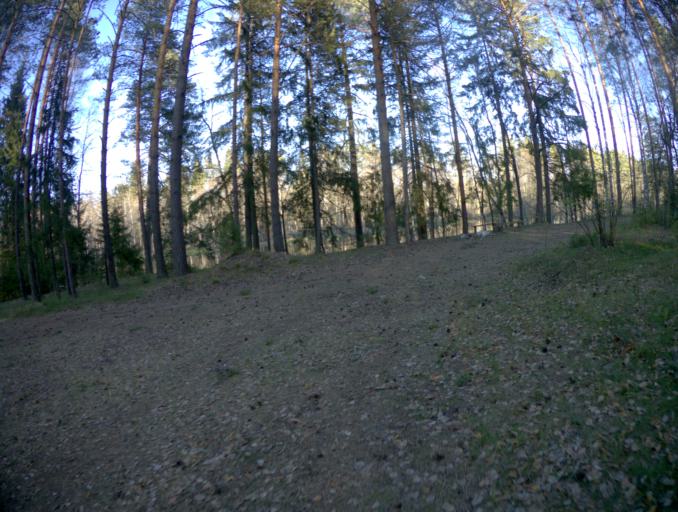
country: RU
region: Vladimir
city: Mezinovskiy
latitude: 55.6119
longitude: 40.3907
